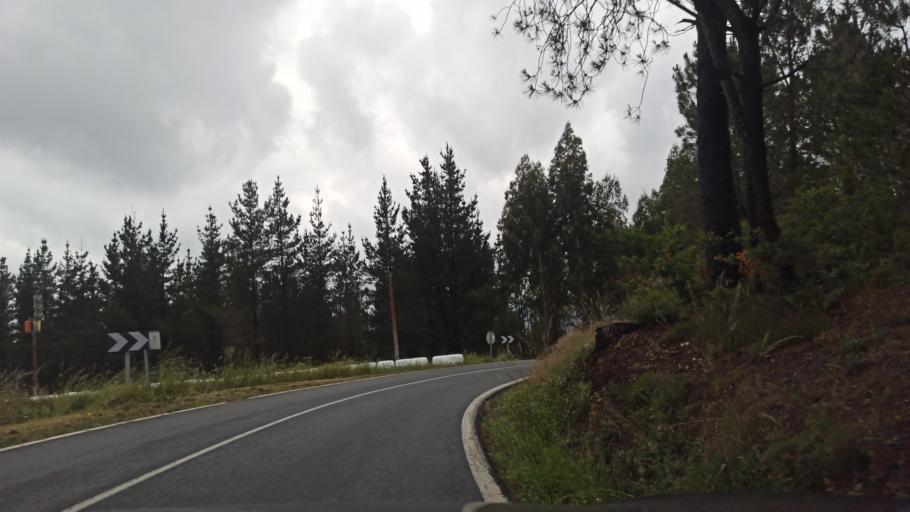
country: ES
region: Galicia
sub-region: Provincia da Coruna
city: Santiso
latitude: 42.7766
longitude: -8.0829
